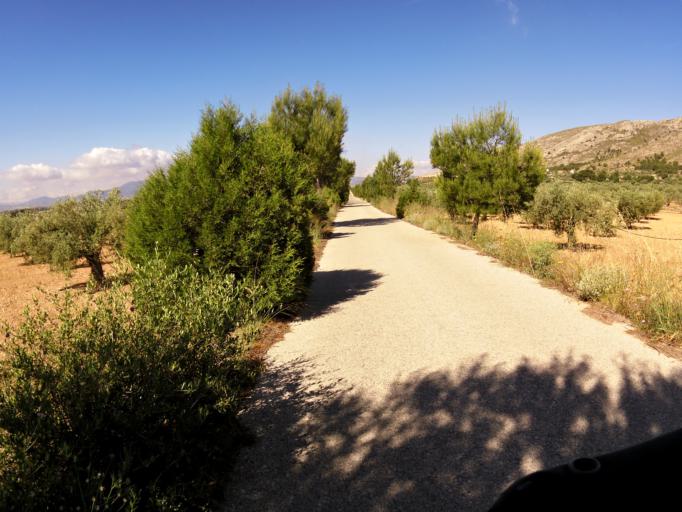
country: ES
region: Valencia
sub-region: Provincia de Alicante
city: Canada
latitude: 38.6395
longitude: -0.8228
